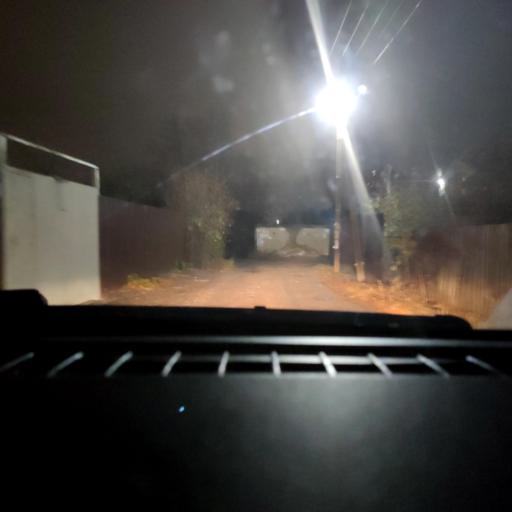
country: RU
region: Voronezj
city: Voronezh
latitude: 51.6703
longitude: 39.2825
